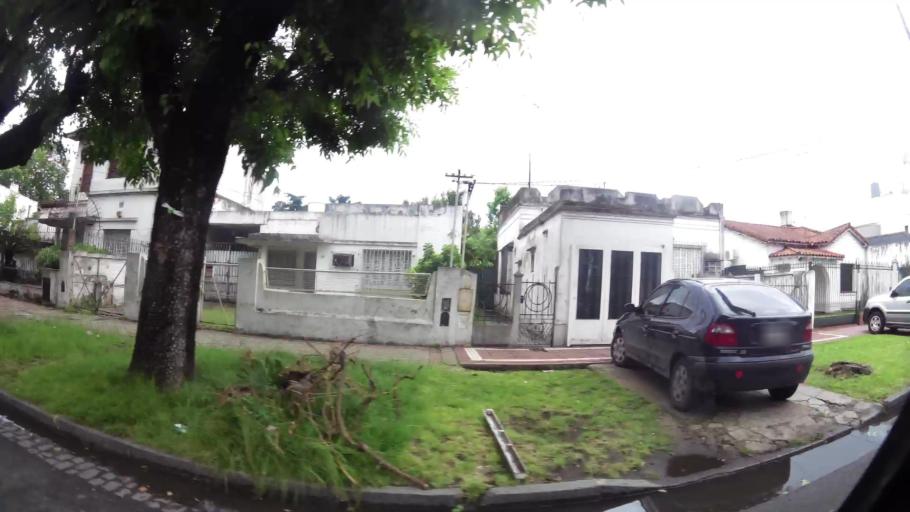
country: AR
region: Buenos Aires
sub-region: Partido de Lomas de Zamora
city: Lomas de Zamora
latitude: -34.7609
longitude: -58.3899
